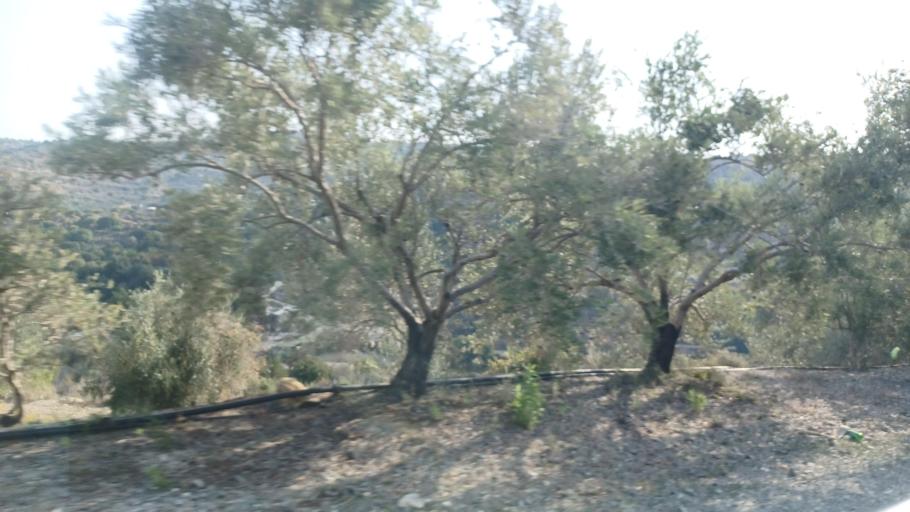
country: CY
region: Pafos
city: Polis
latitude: 34.9807
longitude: 32.4736
